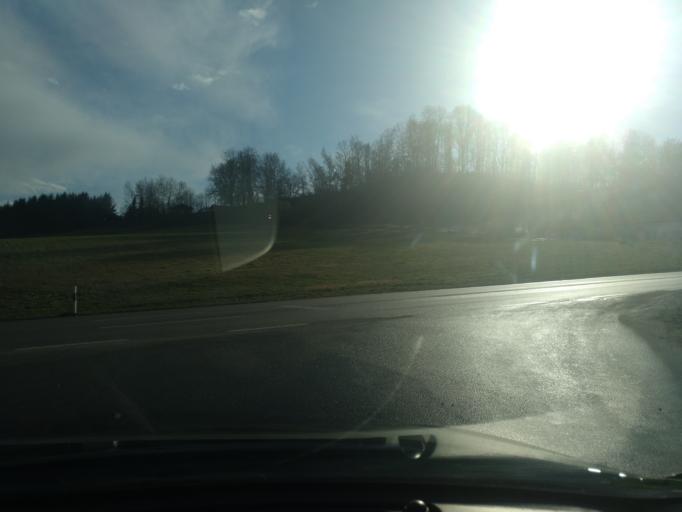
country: DE
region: Bavaria
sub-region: Upper Palatinate
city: Zandt
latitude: 49.1554
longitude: 12.7336
